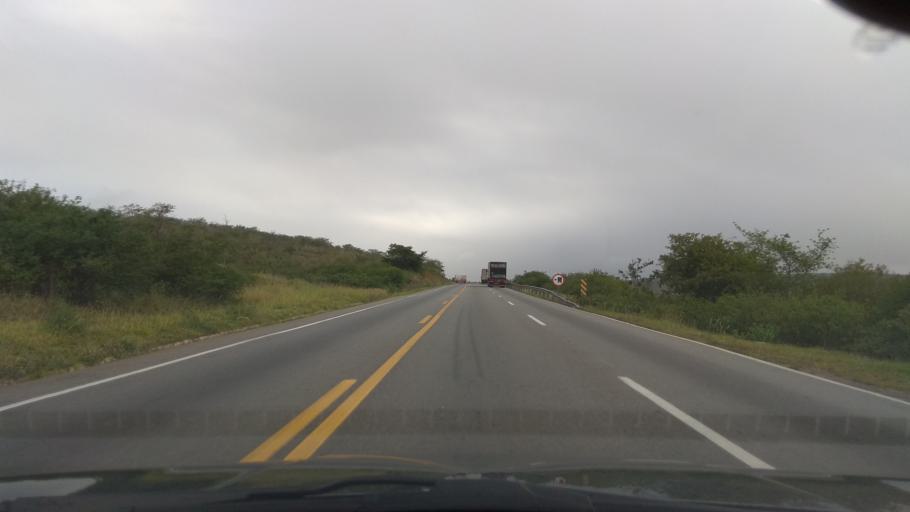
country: BR
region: Bahia
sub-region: Santa Ines
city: Santa Ines
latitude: -13.0356
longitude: -39.9663
